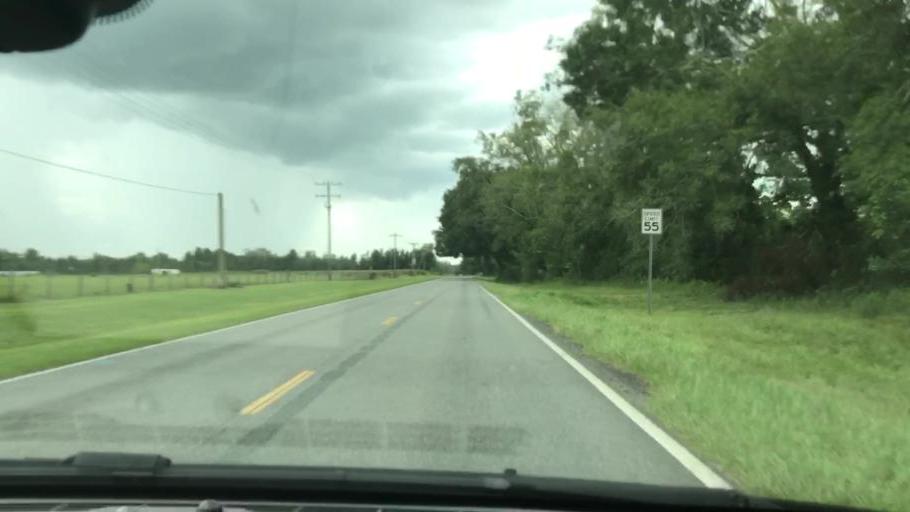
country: US
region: Florida
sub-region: Madison County
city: Madison
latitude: 30.3984
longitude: -83.3004
